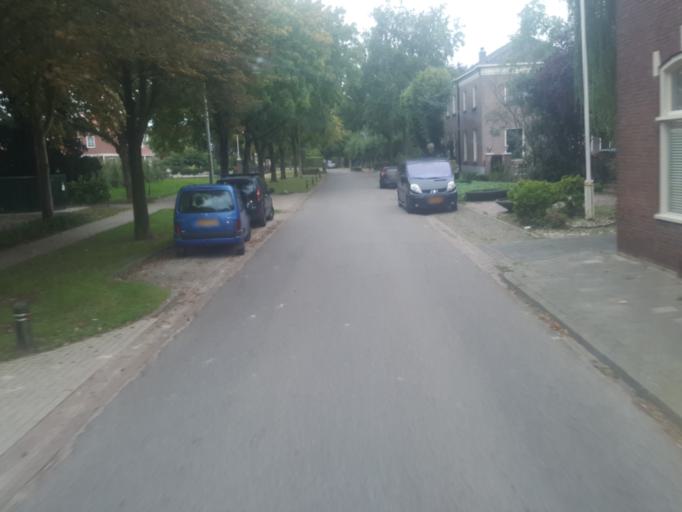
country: NL
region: Gelderland
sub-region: Gemeente Tiel
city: Tiel
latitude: 51.8474
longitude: 5.4295
